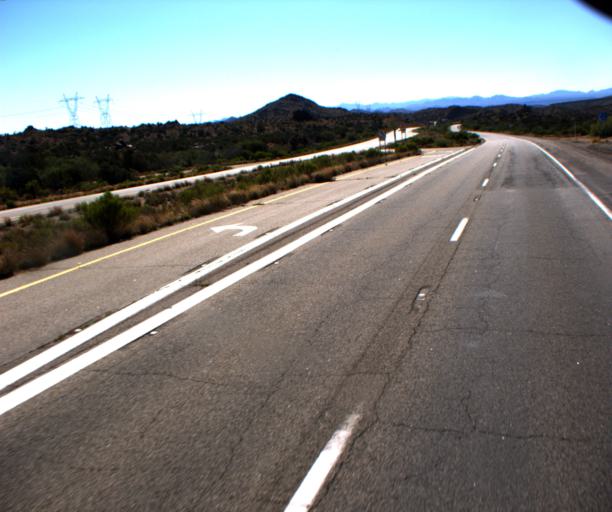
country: US
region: Arizona
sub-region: Yavapai County
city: Bagdad
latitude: 34.4681
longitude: -113.3118
